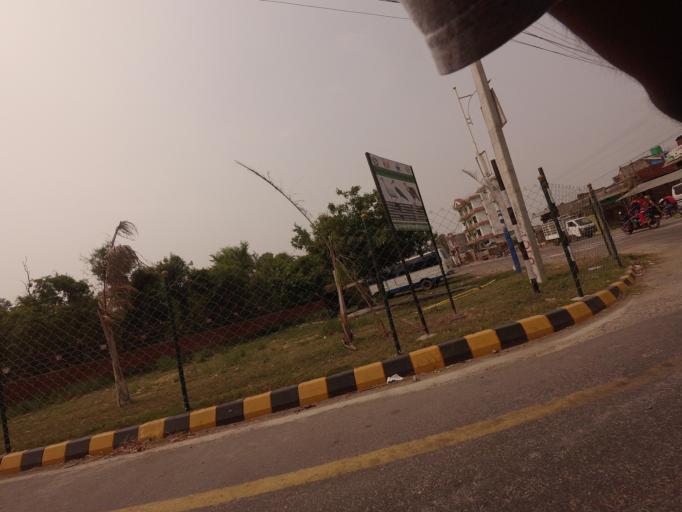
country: IN
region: Uttar Pradesh
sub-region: Maharajganj
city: Nautanwa
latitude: 27.4916
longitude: 83.2682
